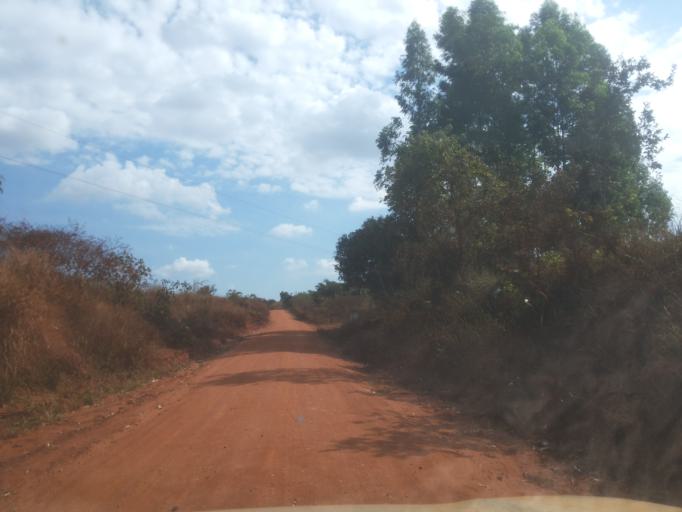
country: BR
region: Minas Gerais
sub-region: Ituiutaba
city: Ituiutaba
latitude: -18.9927
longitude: -49.4219
